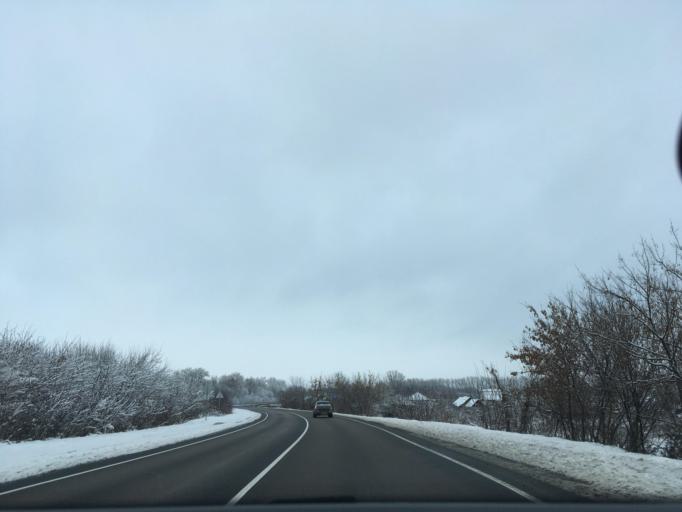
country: RU
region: Voronezj
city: Zabolotovka
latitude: 50.2458
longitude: 39.3718
